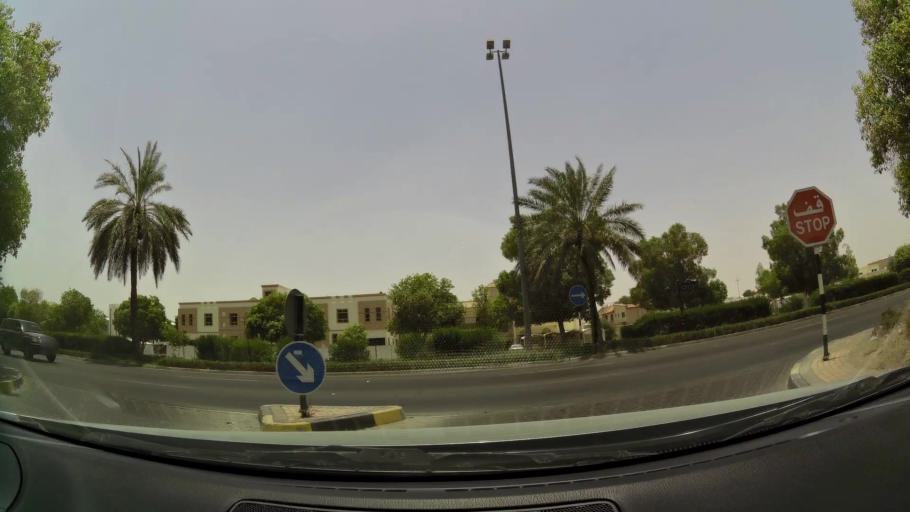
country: AE
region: Abu Dhabi
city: Al Ain
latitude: 24.2056
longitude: 55.7438
